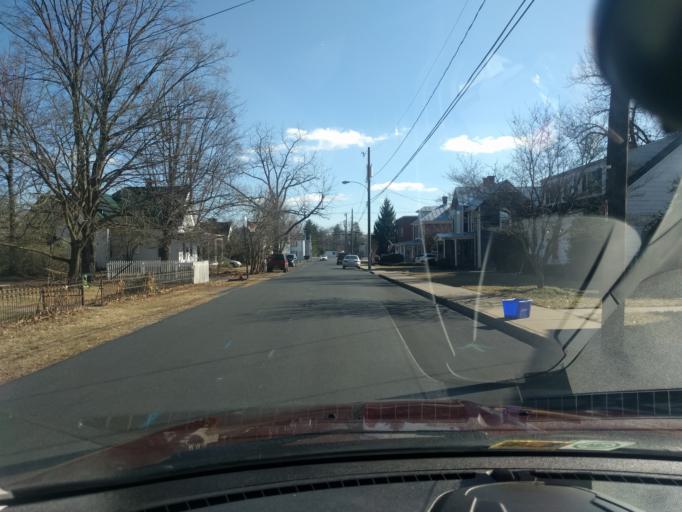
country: US
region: Virginia
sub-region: Rockingham County
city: Bridgewater
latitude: 38.3842
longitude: -78.9770
